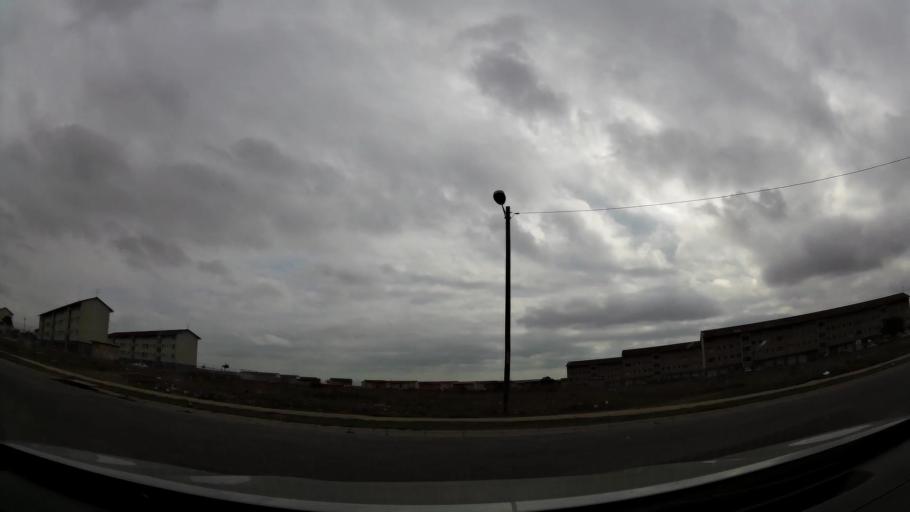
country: ZA
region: Eastern Cape
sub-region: Nelson Mandela Bay Metropolitan Municipality
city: Port Elizabeth
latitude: -33.8958
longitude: 25.5615
